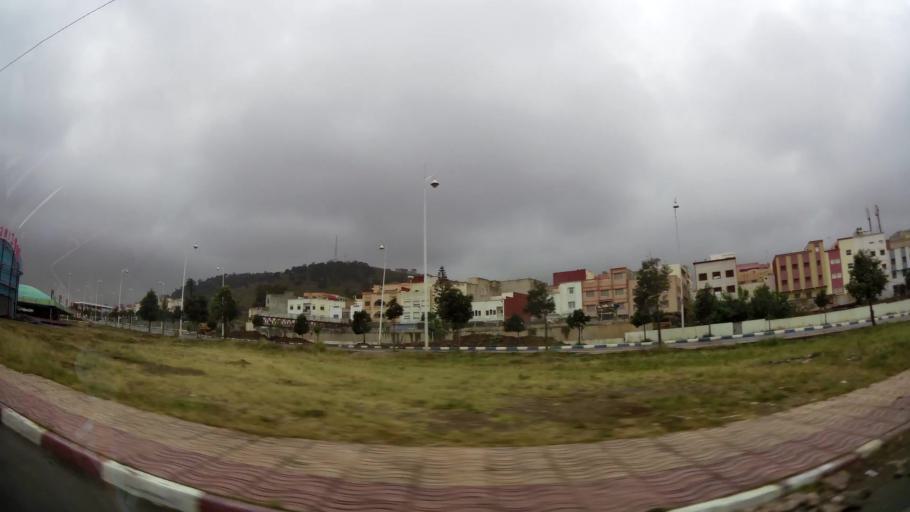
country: MA
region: Oriental
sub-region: Nador
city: Nador
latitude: 35.1871
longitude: -2.9264
